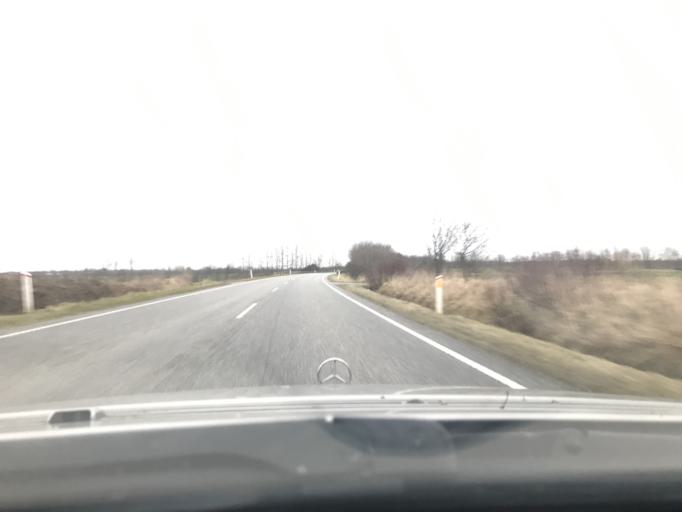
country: DK
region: South Denmark
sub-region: Tonder Kommune
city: Toftlund
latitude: 55.1763
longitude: 8.9969
